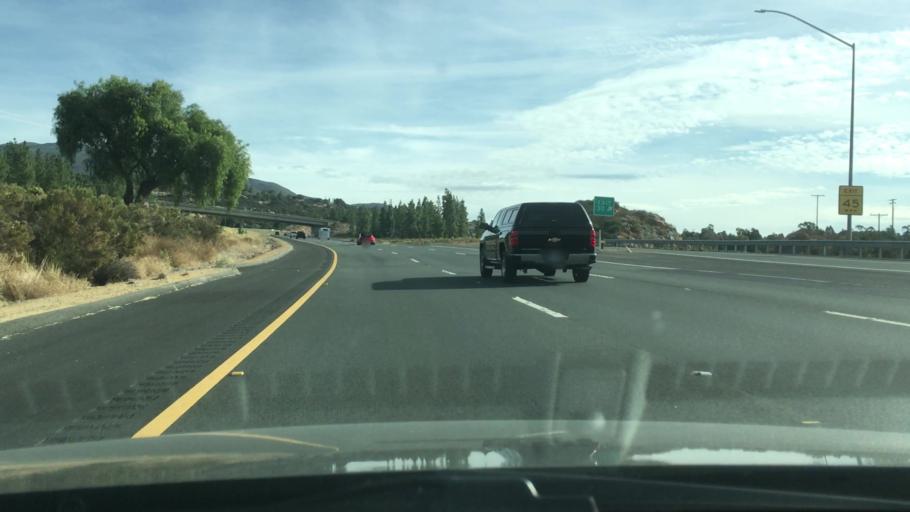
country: US
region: California
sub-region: San Diego County
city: Alpine
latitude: 32.8393
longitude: -116.7839
